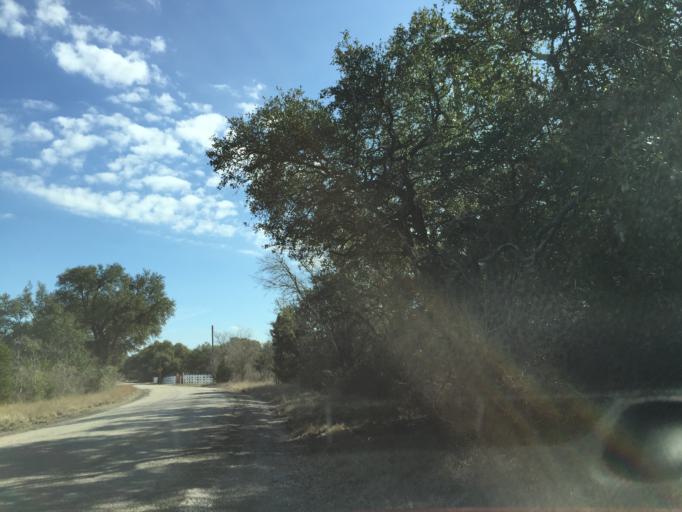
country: US
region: Texas
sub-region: Williamson County
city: Florence
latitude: 30.7746
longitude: -97.8904
